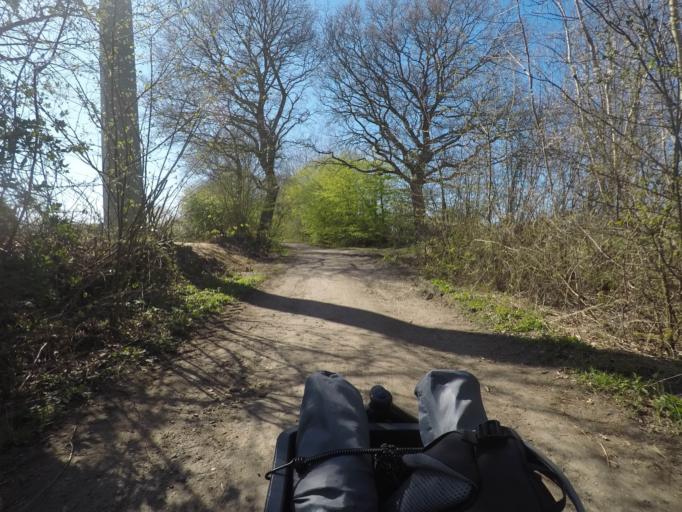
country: DE
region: Schleswig-Holstein
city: Stapelfeld
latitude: 53.6004
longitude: 10.1940
